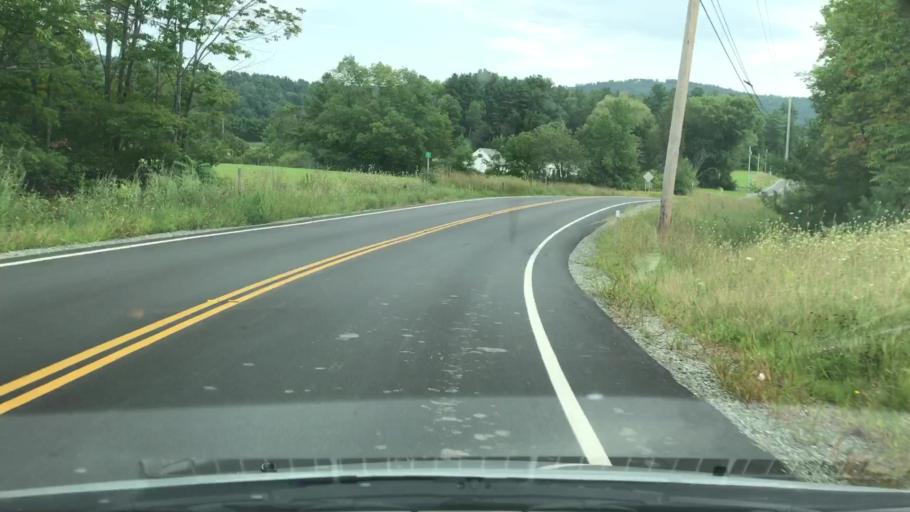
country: US
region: New Hampshire
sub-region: Grafton County
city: Lyme Town Offices
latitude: 43.8421
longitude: -72.1527
